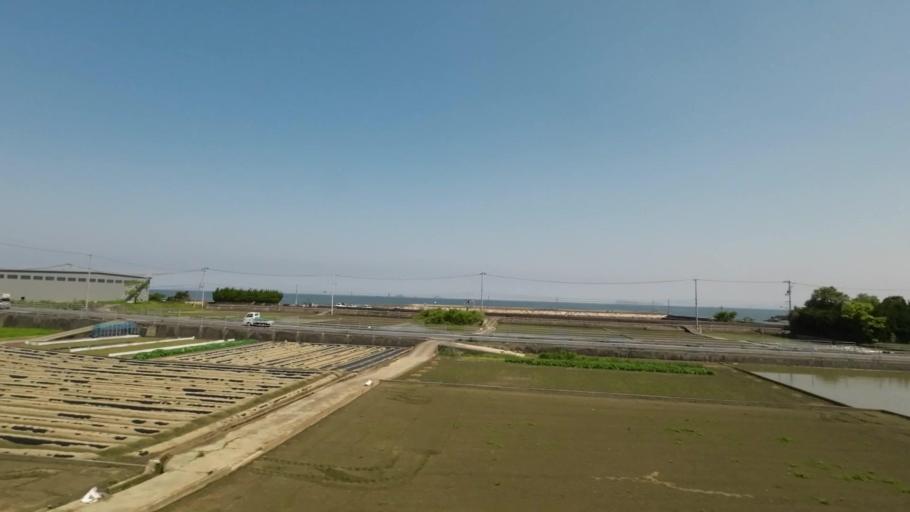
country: JP
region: Ehime
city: Kawanoecho
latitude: 33.9705
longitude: 133.4807
